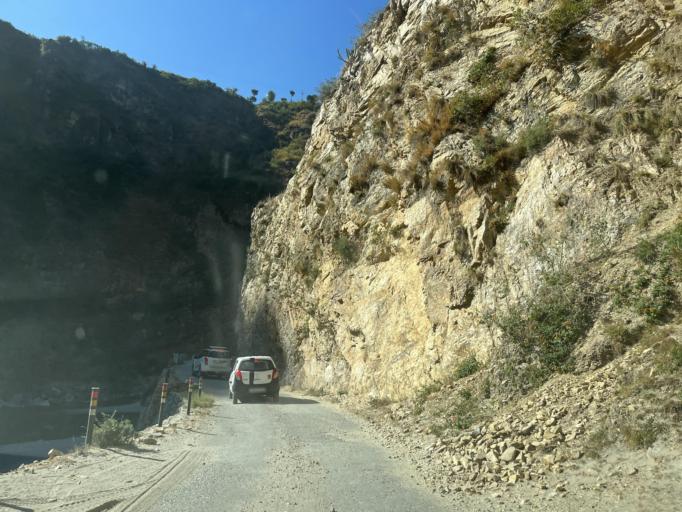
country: IN
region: Uttarakhand
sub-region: Naini Tal
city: Naini Tal
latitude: 29.5064
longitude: 79.4539
